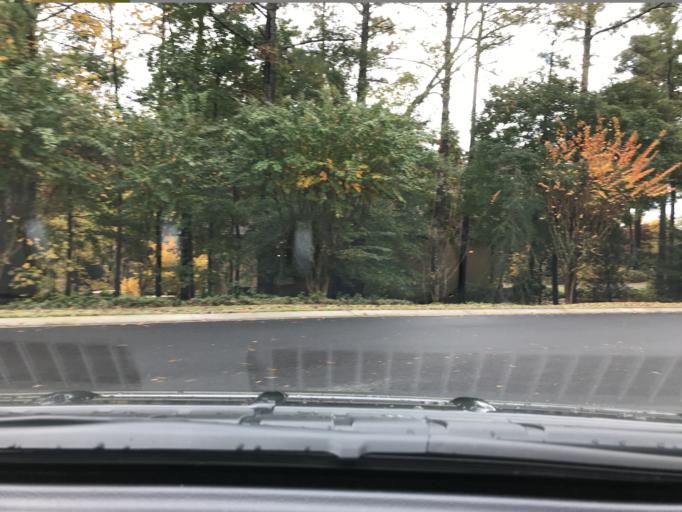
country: US
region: Georgia
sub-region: Fulton County
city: Johns Creek
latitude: 34.0117
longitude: -84.2470
